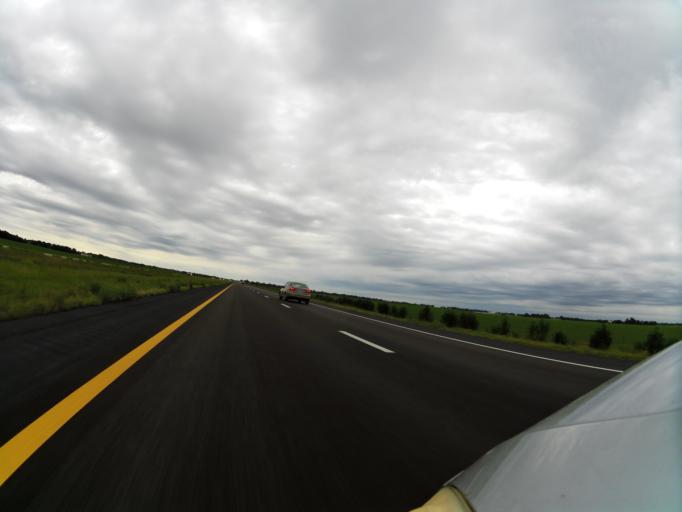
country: US
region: Kansas
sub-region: Reno County
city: Haven
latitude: 37.8762
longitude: -97.6563
